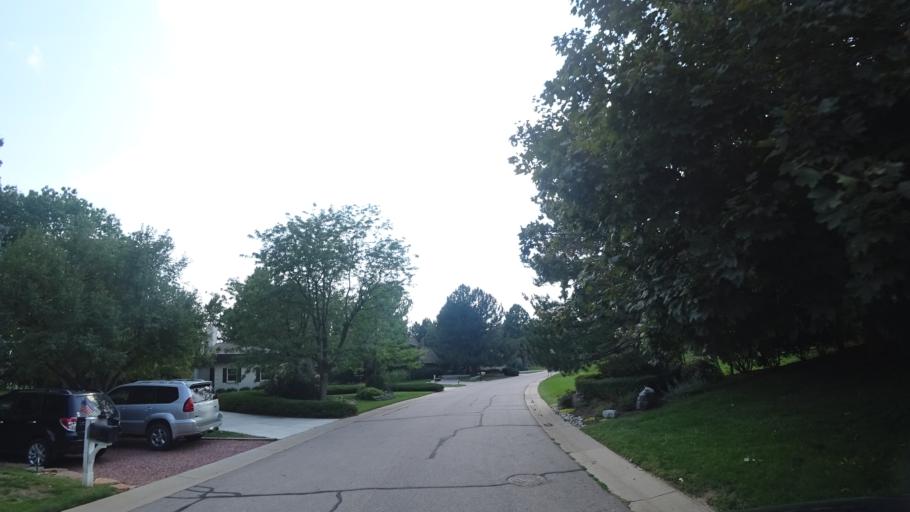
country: US
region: Colorado
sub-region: Arapahoe County
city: Greenwood Village
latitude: 39.6118
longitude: -104.9622
